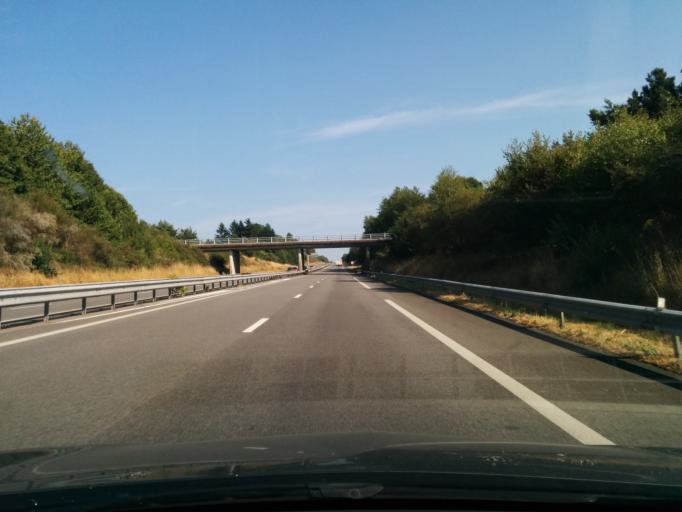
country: FR
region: Limousin
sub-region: Departement de la Haute-Vienne
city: Saint-Germain-les-Belles
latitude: 45.5852
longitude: 1.4722
